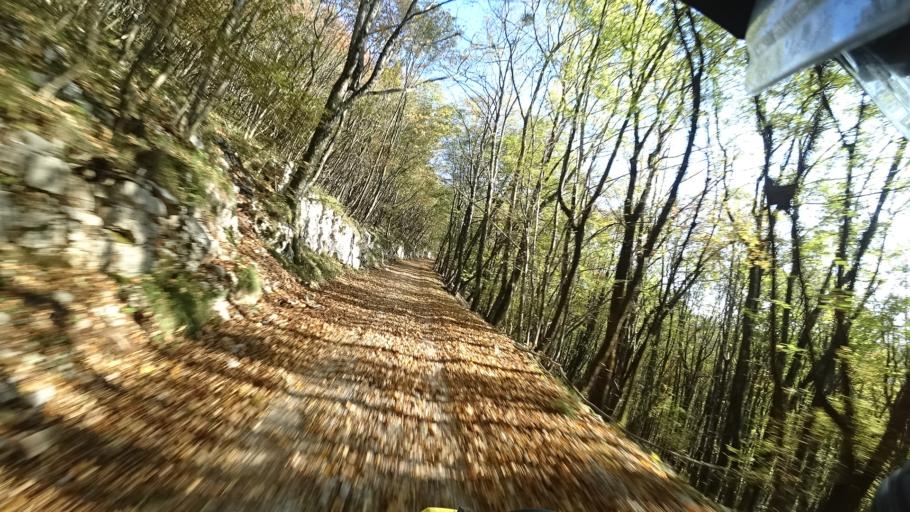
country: HR
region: Primorsko-Goranska
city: Klana
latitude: 45.4869
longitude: 14.4136
